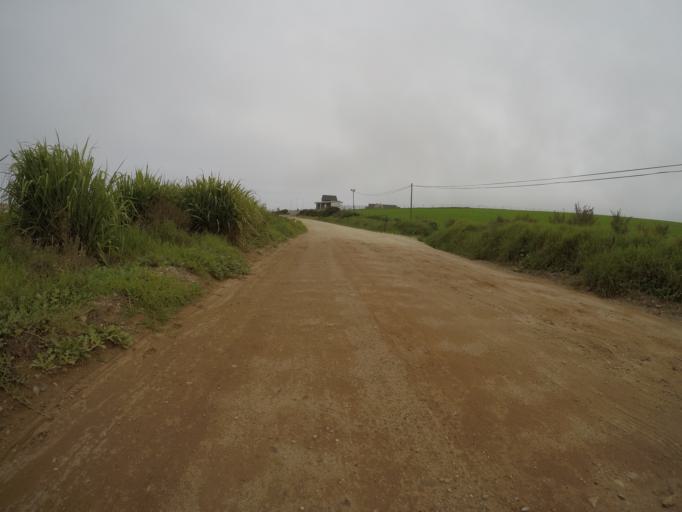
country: ZA
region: Eastern Cape
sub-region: Cacadu District Municipality
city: Kareedouw
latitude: -34.0703
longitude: 24.2358
